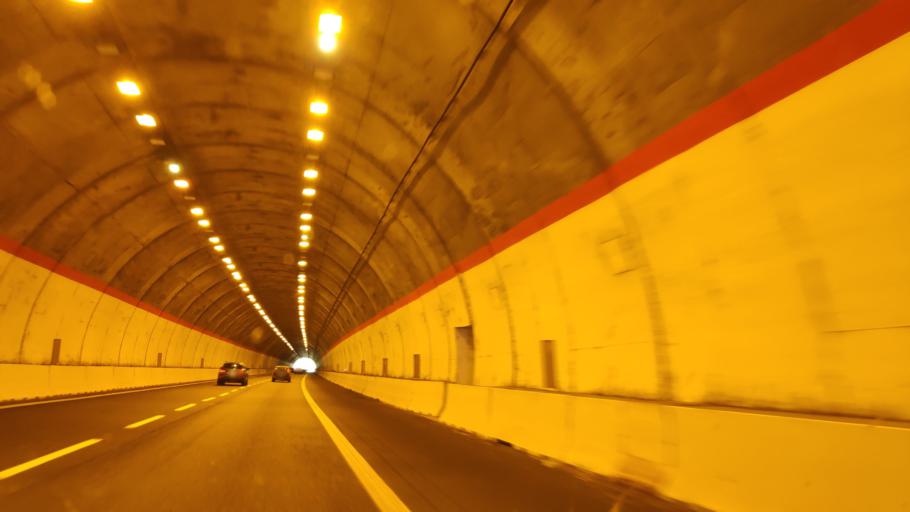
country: IT
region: Campania
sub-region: Provincia di Salerno
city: Auletta
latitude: 40.5337
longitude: 15.4239
